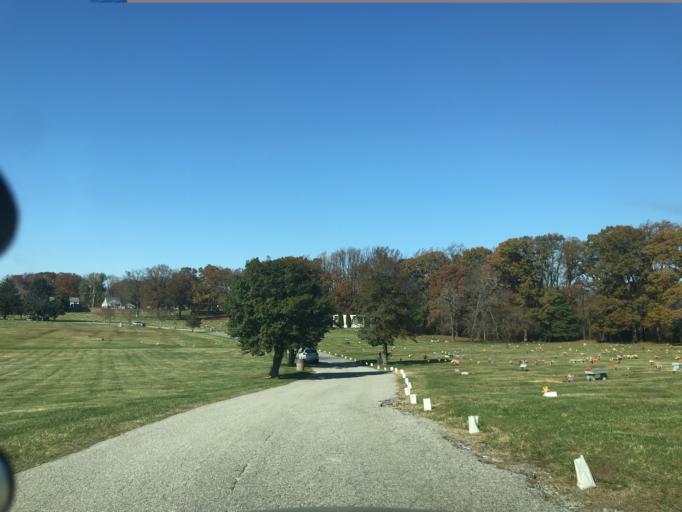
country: US
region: Maryland
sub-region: Baltimore County
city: White Marsh
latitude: 39.3596
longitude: -76.4220
